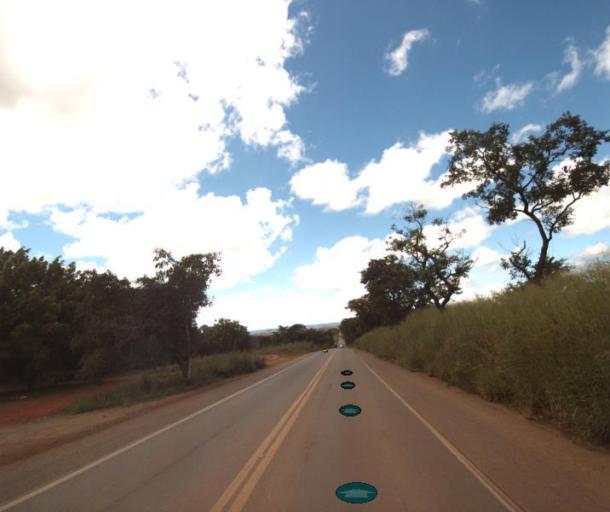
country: BR
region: Goias
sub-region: Petrolina De Goias
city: Petrolina de Goias
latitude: -15.9839
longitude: -49.1582
